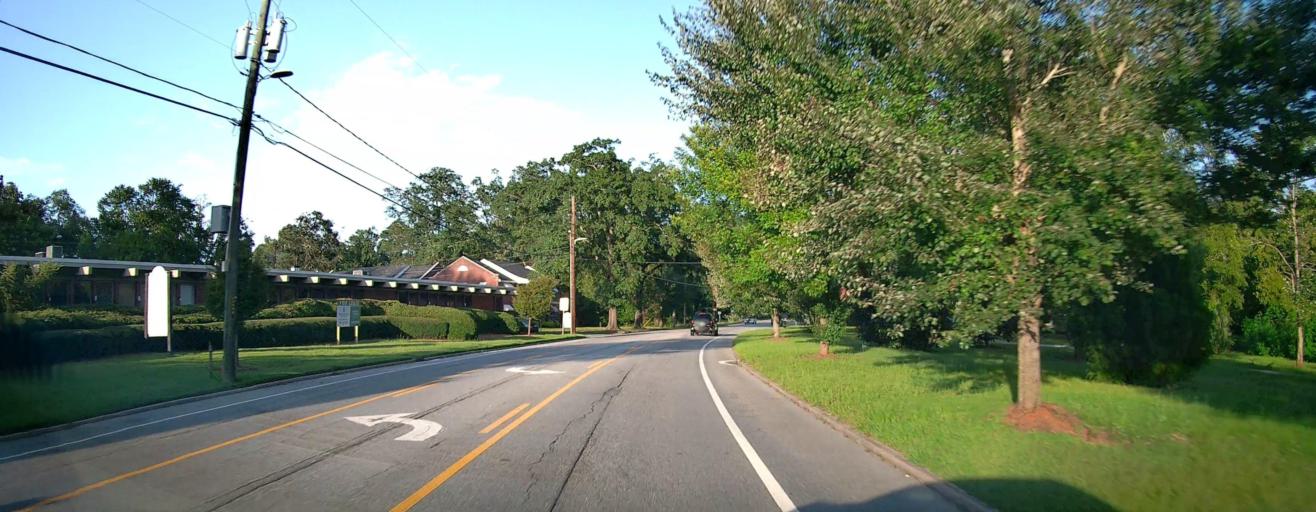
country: US
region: Georgia
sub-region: Muscogee County
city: Columbus
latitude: 32.4718
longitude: -84.9688
